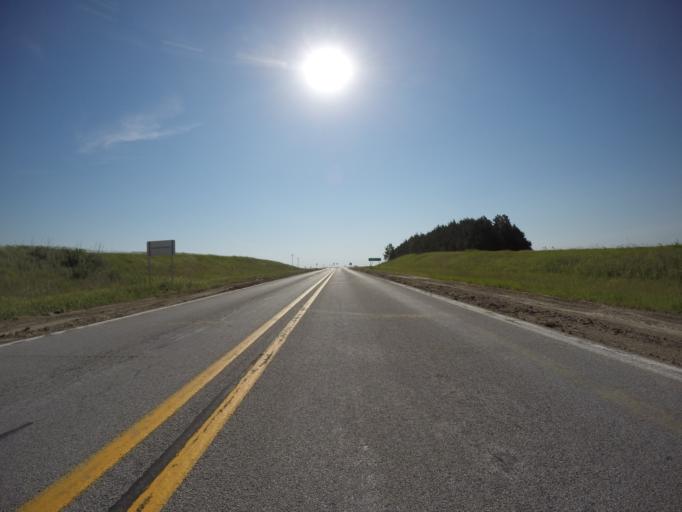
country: US
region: Nebraska
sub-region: Pawnee County
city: Pawnee City
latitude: 40.0446
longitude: -96.3528
